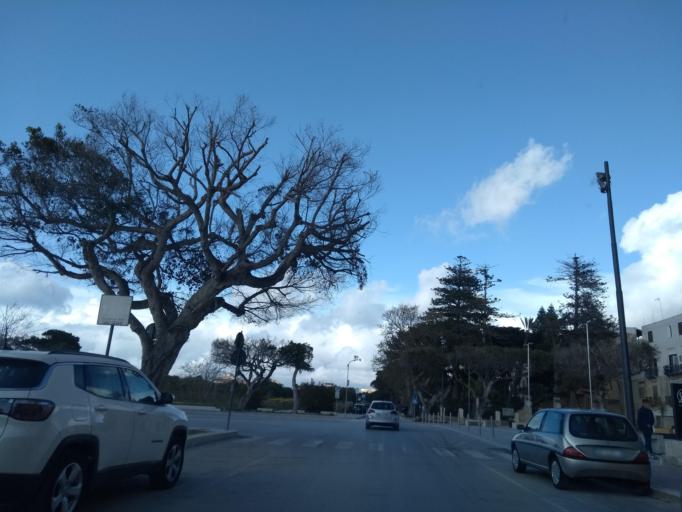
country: IT
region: Sicily
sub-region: Trapani
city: Marsala
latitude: 37.8013
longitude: 12.4311
